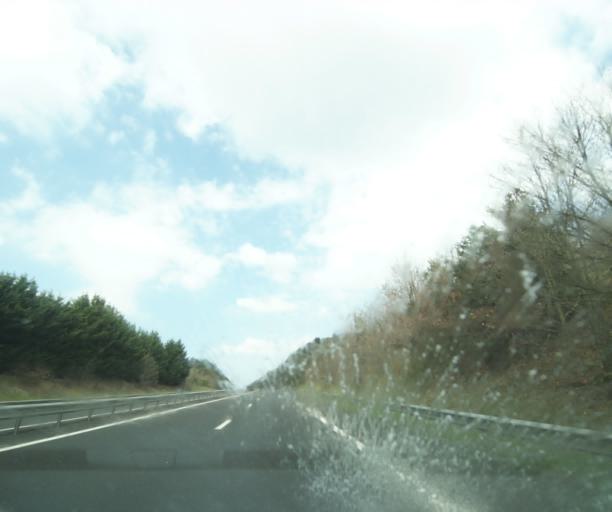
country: FR
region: Auvergne
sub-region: Departement du Cantal
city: Massiac
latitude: 45.2446
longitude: 3.2044
